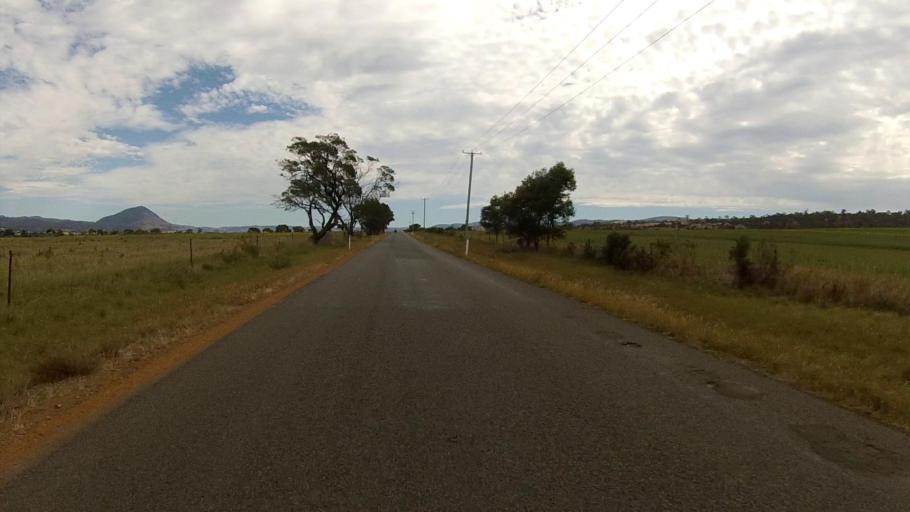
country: AU
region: Tasmania
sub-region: Clarence
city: Cambridge
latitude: -42.7257
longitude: 147.4498
